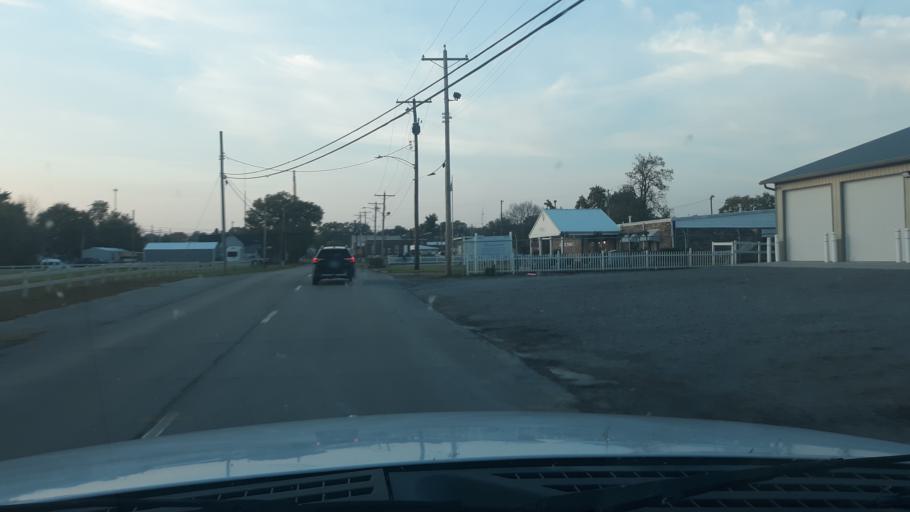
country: US
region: Illinois
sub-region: Saline County
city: Eldorado
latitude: 37.8107
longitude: -88.4360
